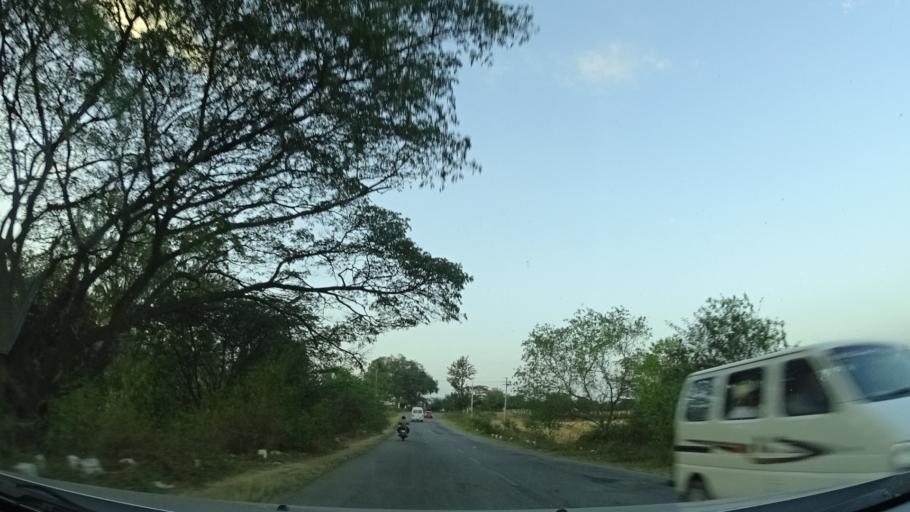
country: IN
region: Karnataka
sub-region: Ramanagara
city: Kanakapura
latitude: 12.6261
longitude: 77.4312
